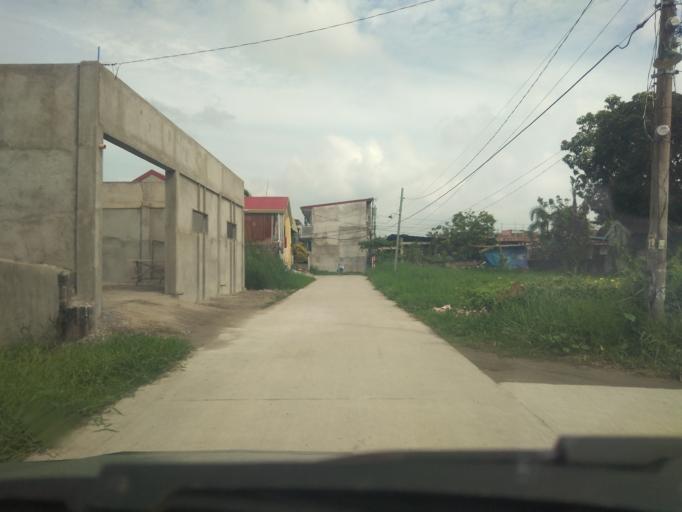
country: PH
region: Central Luzon
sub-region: Province of Pampanga
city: Pau
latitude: 15.0055
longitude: 120.7140
